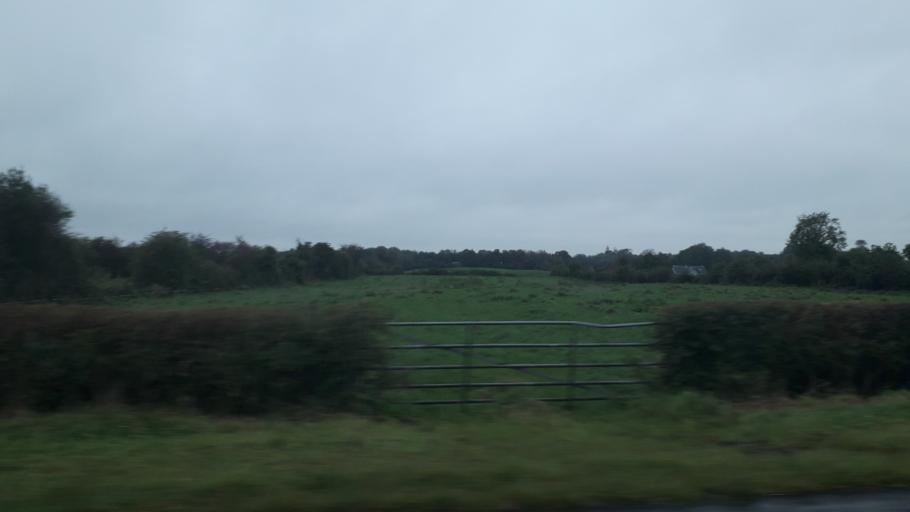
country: IE
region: Leinster
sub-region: An Longfort
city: Edgeworthstown
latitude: 53.6654
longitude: -7.5332
